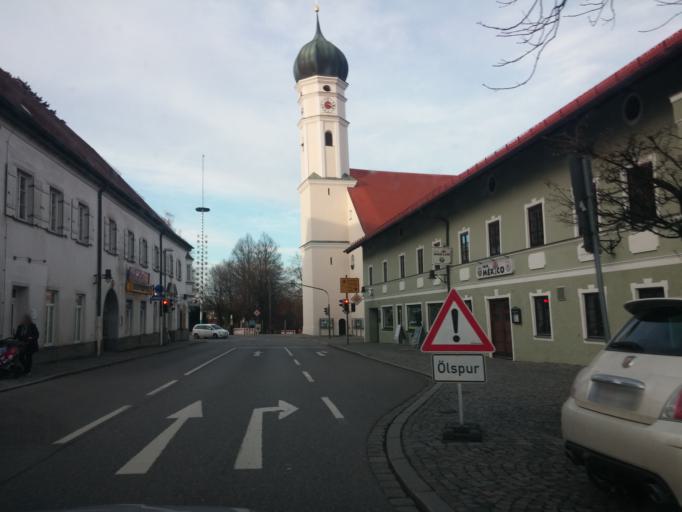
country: DE
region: Bavaria
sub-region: Upper Bavaria
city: Markt Schwaben
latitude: 48.1905
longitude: 11.8689
